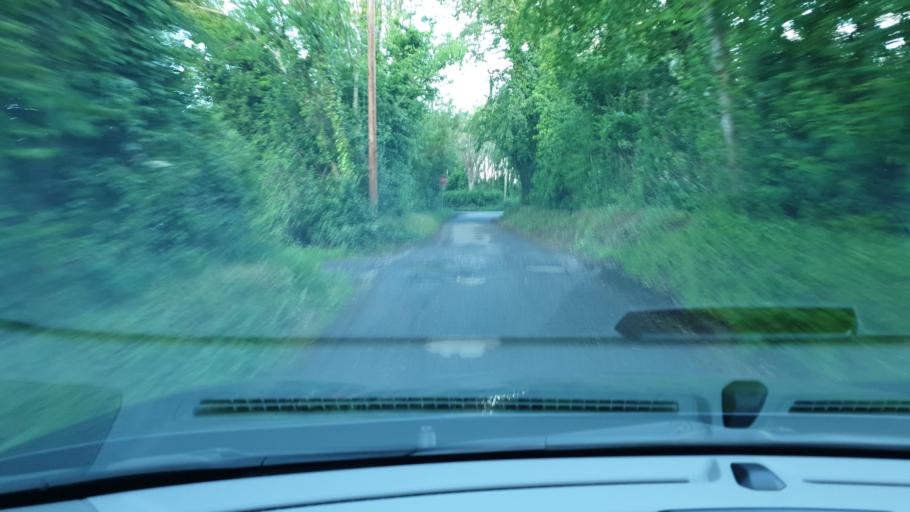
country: IE
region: Leinster
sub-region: An Mhi
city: Ashbourne
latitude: 53.4759
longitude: -6.3380
